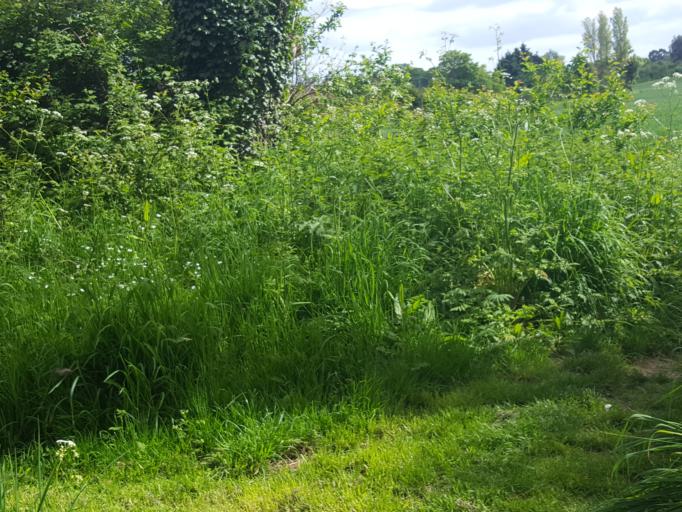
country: GB
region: England
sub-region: Essex
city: Frinton-on-Sea
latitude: 51.8526
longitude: 1.2213
